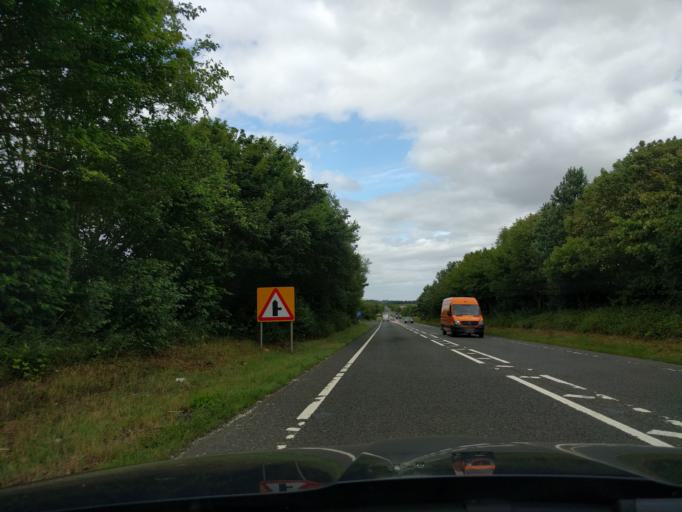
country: GB
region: England
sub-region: Northumberland
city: Alnwick
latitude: 55.4589
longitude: -1.7084
